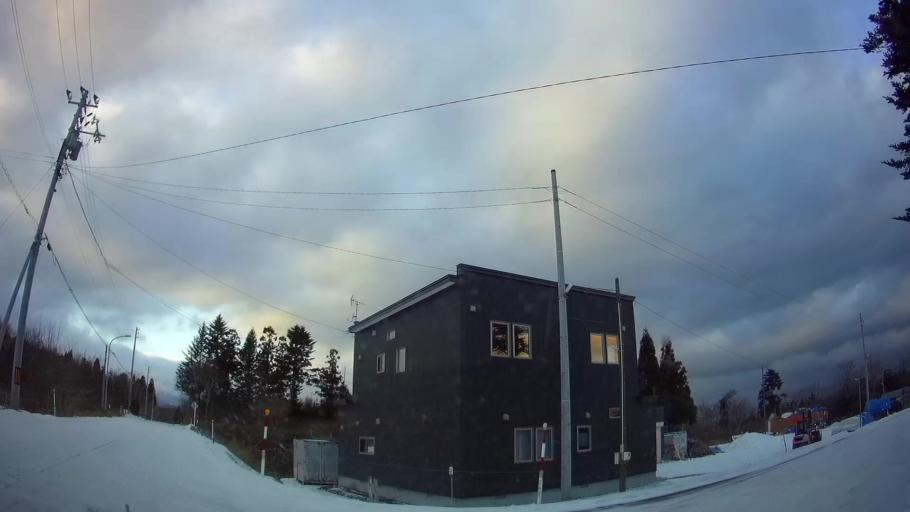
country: JP
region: Hokkaido
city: Nanae
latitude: 42.0217
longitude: 140.8367
